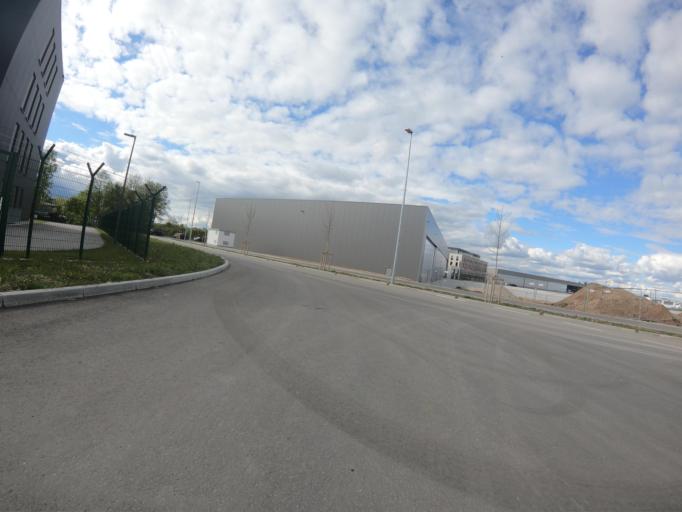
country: DE
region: Bavaria
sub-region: Upper Bavaria
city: Gilching
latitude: 48.0870
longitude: 11.2834
